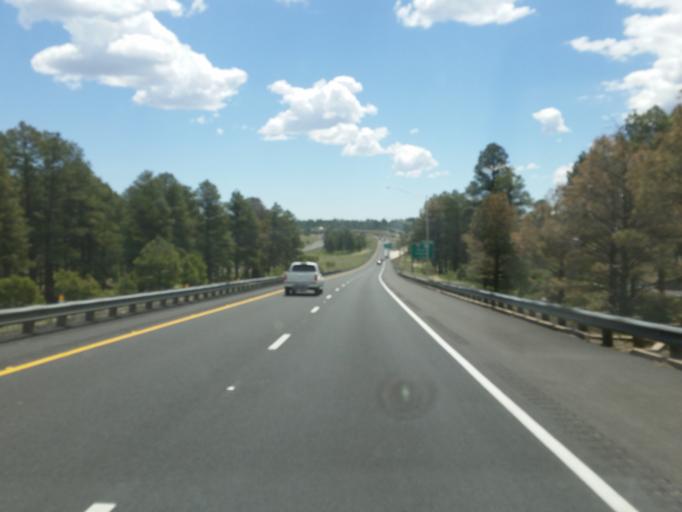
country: US
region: Arizona
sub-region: Coconino County
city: Flagstaff
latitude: 35.1759
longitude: -111.6735
